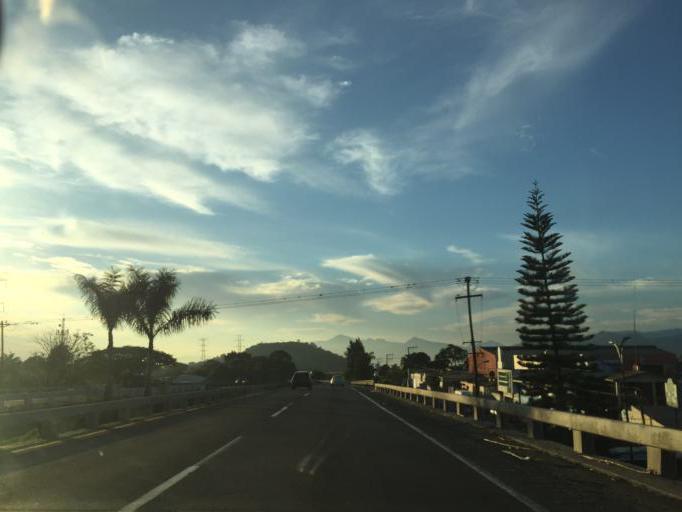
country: MX
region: Veracruz
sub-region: Fortin
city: Cordoba (Santa Leticia)
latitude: 18.9029
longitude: -96.9858
